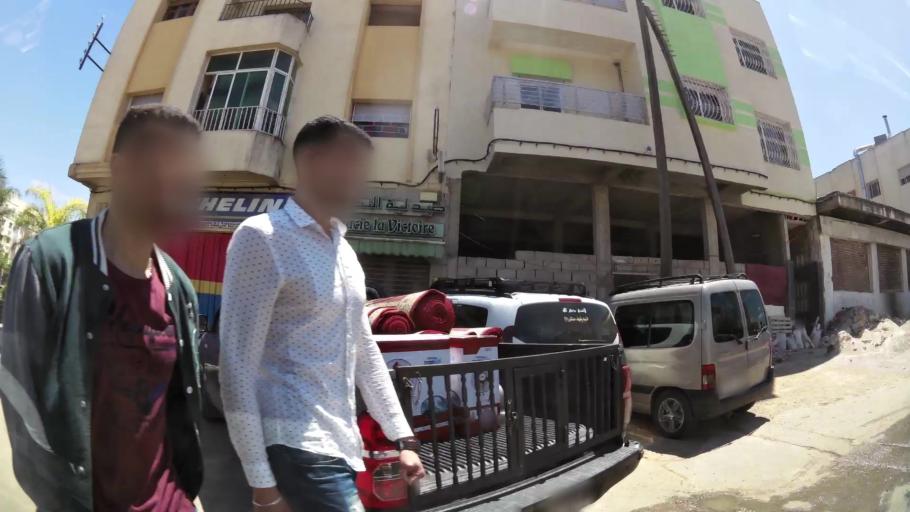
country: MA
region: Fes-Boulemane
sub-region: Fes
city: Fes
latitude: 34.0179
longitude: -4.9862
